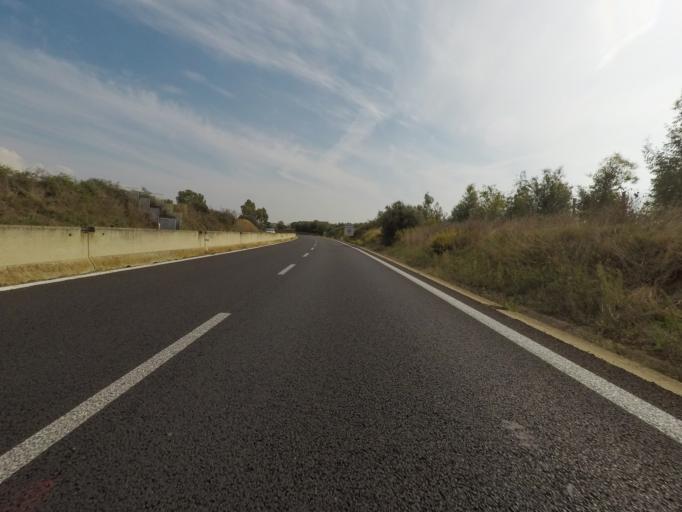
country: IT
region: Latium
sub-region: Provincia di Viterbo
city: Pescia Romana
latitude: 42.4098
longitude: 11.4779
